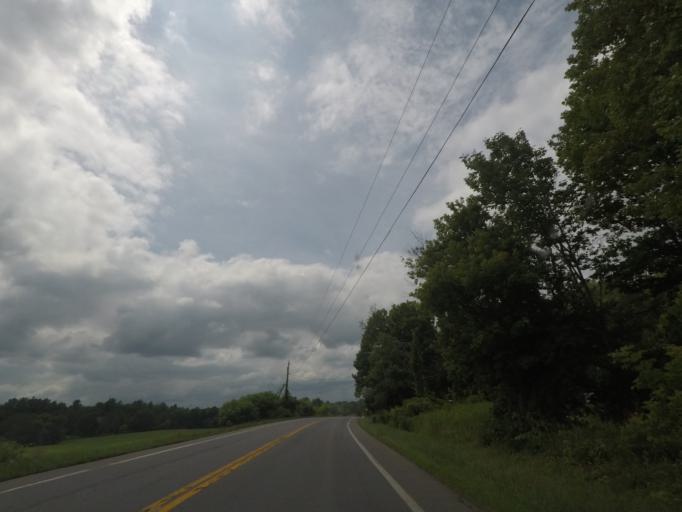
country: US
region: New York
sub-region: Saratoga County
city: Saratoga Springs
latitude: 43.0688
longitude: -73.6874
